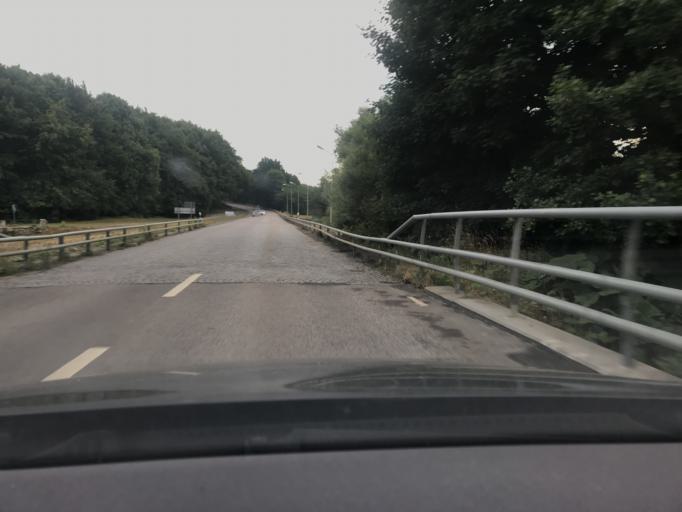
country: SE
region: Skane
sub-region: Simrishamns Kommun
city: Simrishamn
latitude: 55.5704
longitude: 14.3344
